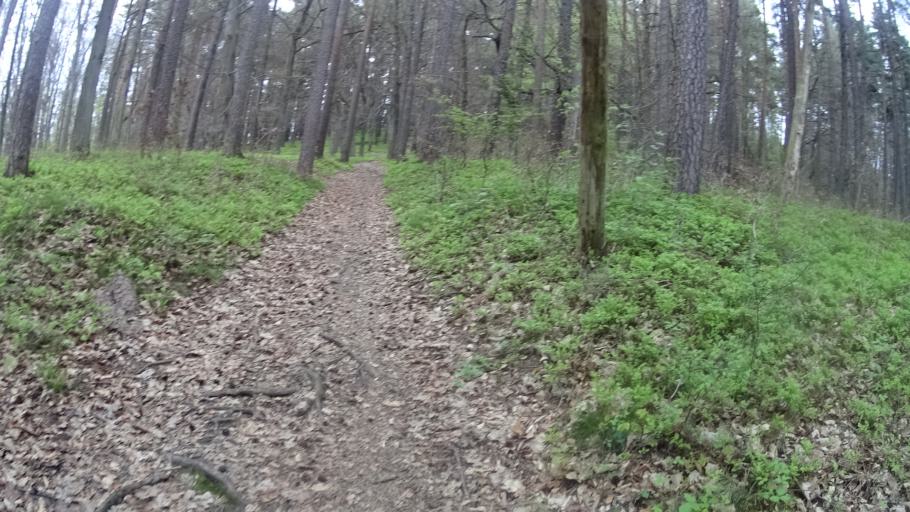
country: DE
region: Bavaria
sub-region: Upper Franconia
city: Kleinsendelbach
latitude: 49.6169
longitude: 11.1801
